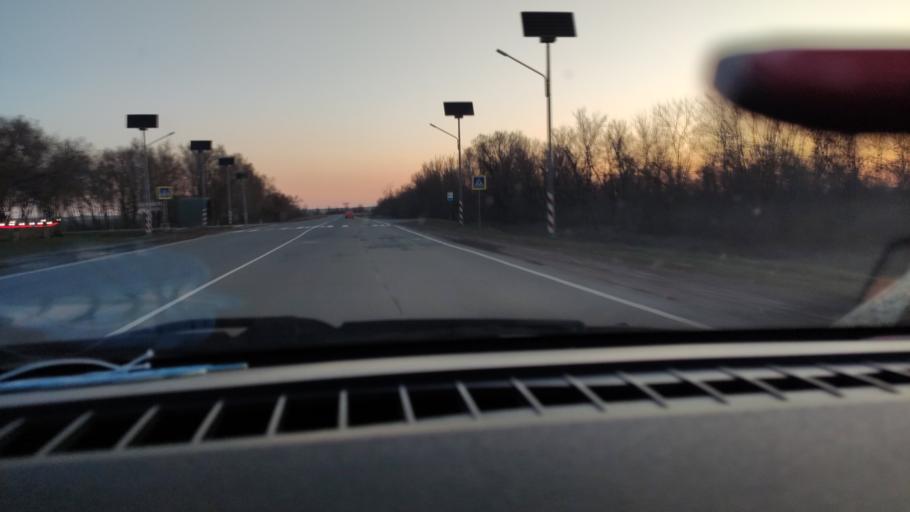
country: RU
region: Saratov
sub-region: Saratovskiy Rayon
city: Saratov
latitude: 51.7040
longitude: 46.0130
